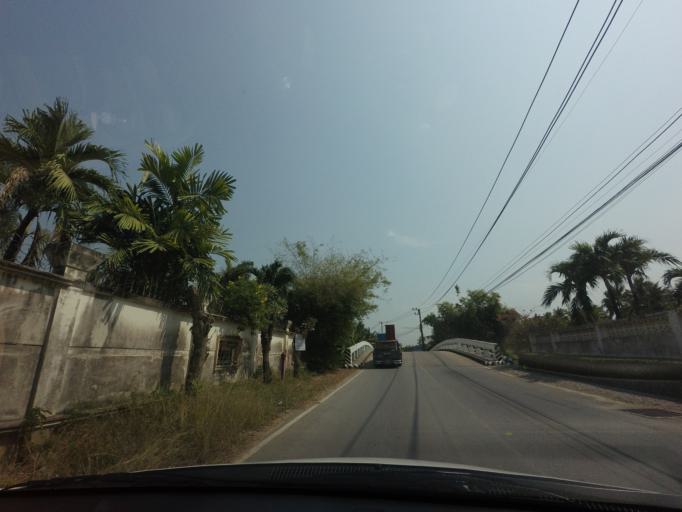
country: TH
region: Nakhon Pathom
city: Sam Phran
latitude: 13.7584
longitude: 100.2488
